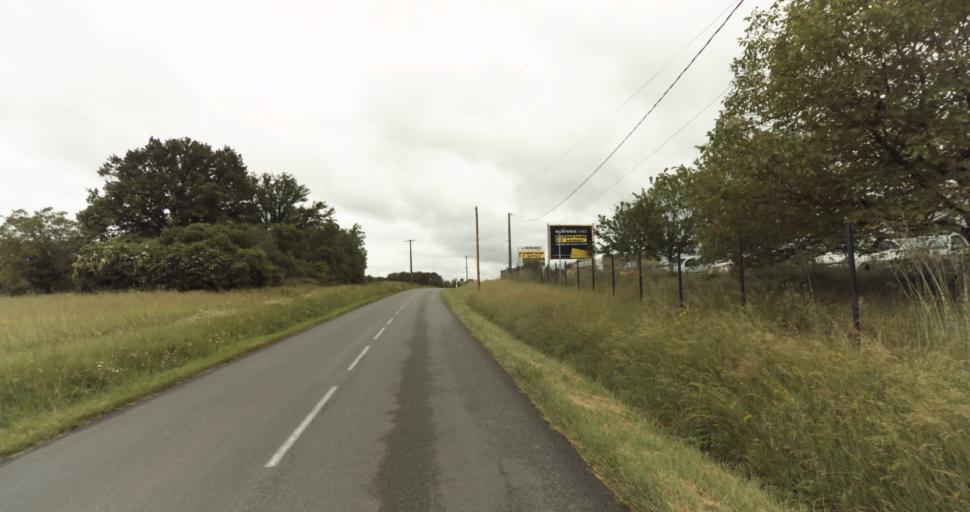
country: FR
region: Aquitaine
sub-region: Departement de la Dordogne
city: Belves
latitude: 44.6894
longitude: 0.9063
